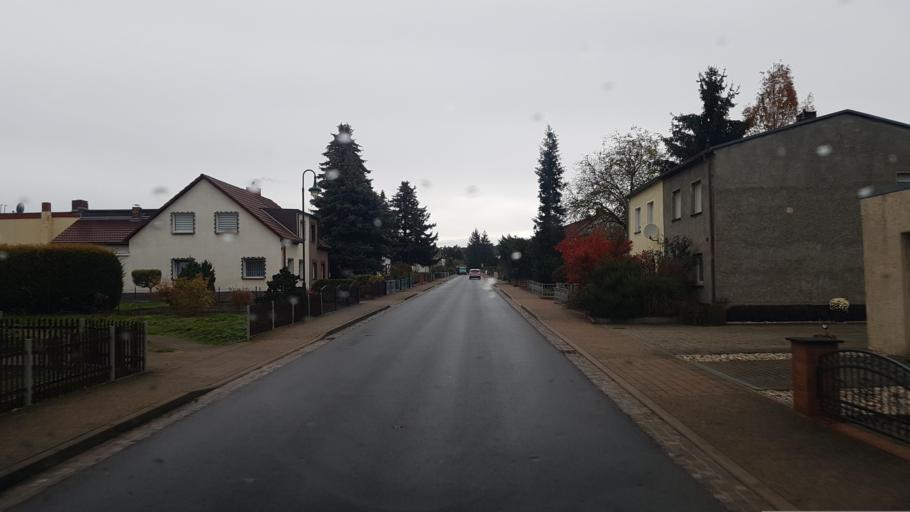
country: DE
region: Saxony-Anhalt
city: Abtsdorf
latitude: 51.8799
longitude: 12.7377
